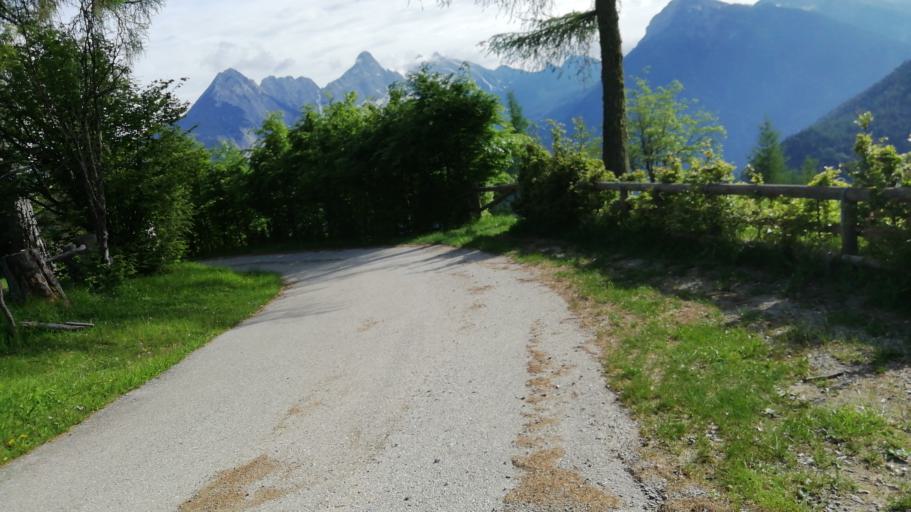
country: IT
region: Veneto
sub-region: Provincia di Belluno
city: Valle di Cadore
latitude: 46.4273
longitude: 12.3182
